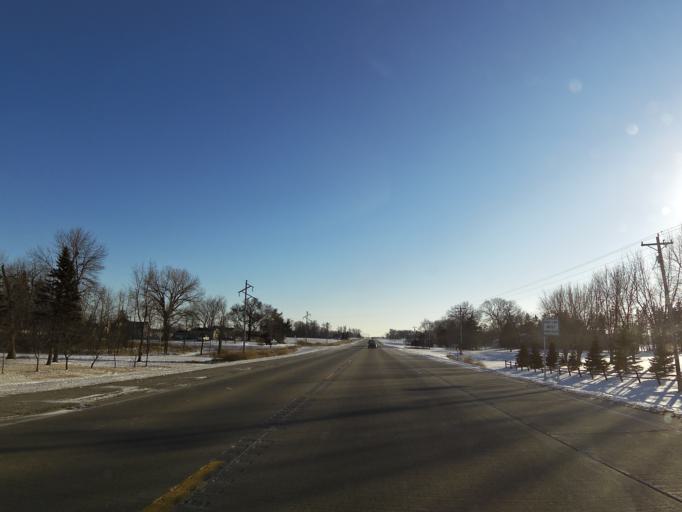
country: US
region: Minnesota
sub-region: Le Sueur County
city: New Prague
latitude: 44.5019
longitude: -93.5856
